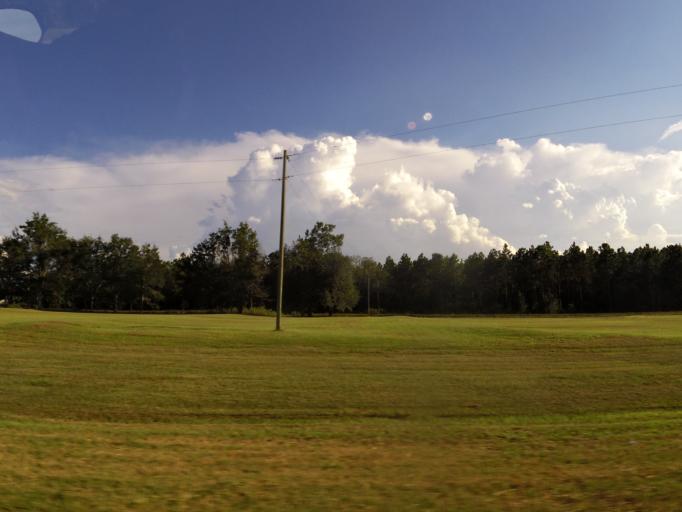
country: US
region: Georgia
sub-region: Brooks County
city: Quitman
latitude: 30.7908
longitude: -83.4811
